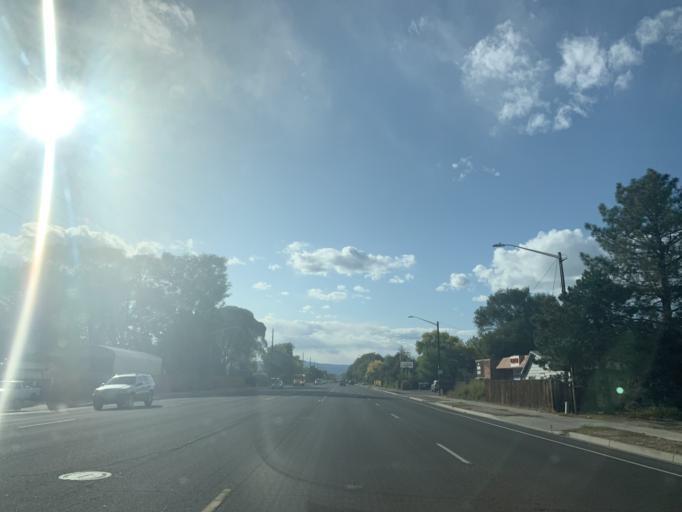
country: US
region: Colorado
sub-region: Mesa County
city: Fruitvale
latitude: 39.0918
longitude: -108.4908
